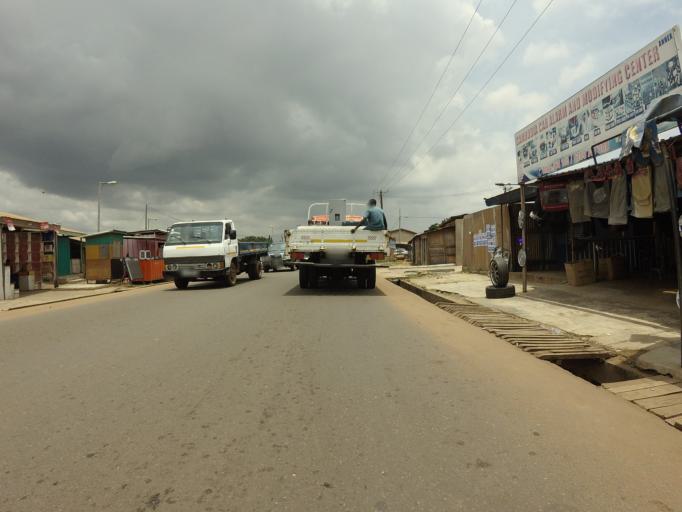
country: GH
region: Greater Accra
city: Medina Estates
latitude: 5.6779
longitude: -0.1500
